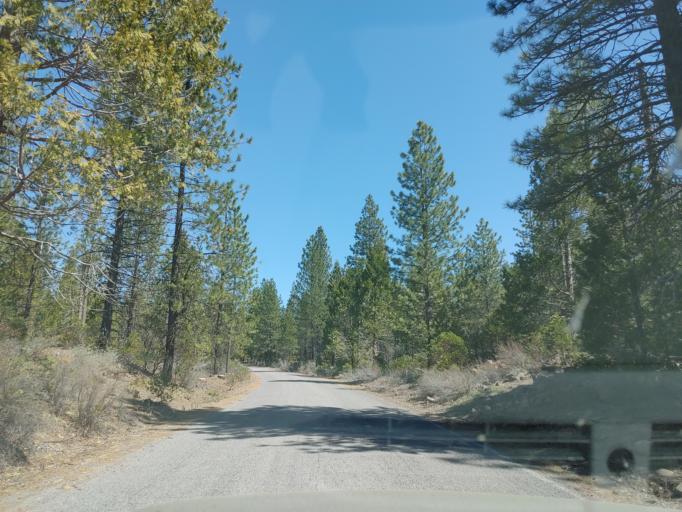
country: US
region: California
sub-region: Siskiyou County
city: McCloud
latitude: 41.2412
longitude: -121.9724
